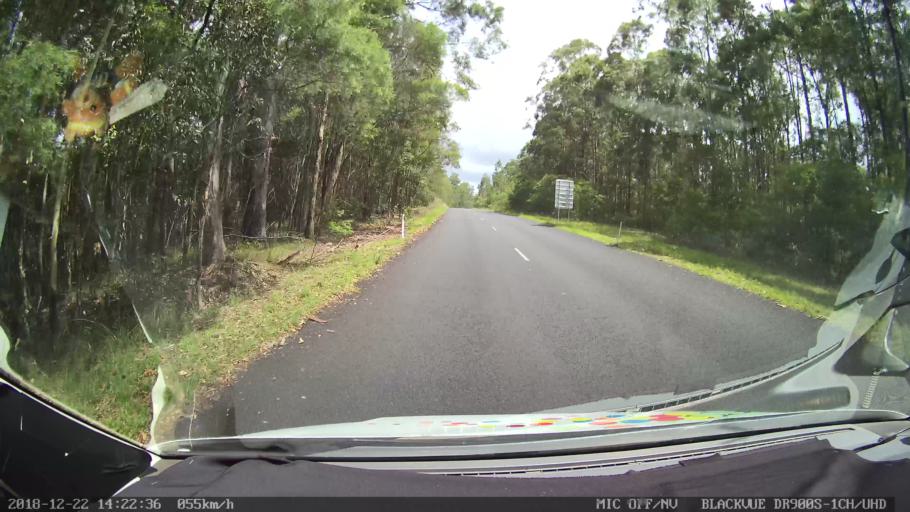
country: AU
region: New South Wales
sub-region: Clarence Valley
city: Coutts Crossing
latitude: -30.0272
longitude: 152.6535
